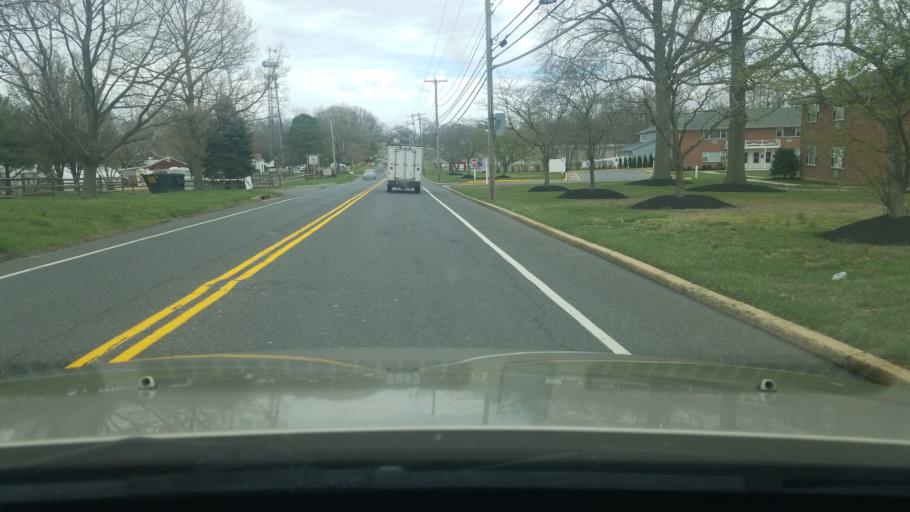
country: US
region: New Jersey
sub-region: Monmouth County
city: Manasquan
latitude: 40.1337
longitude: -74.0703
